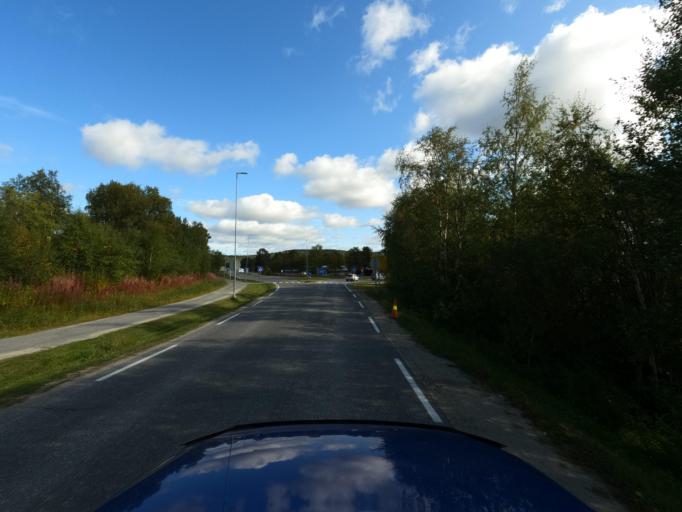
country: NO
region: Finnmark Fylke
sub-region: Karasjok
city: Karasjohka
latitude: 69.4722
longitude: 25.5016
